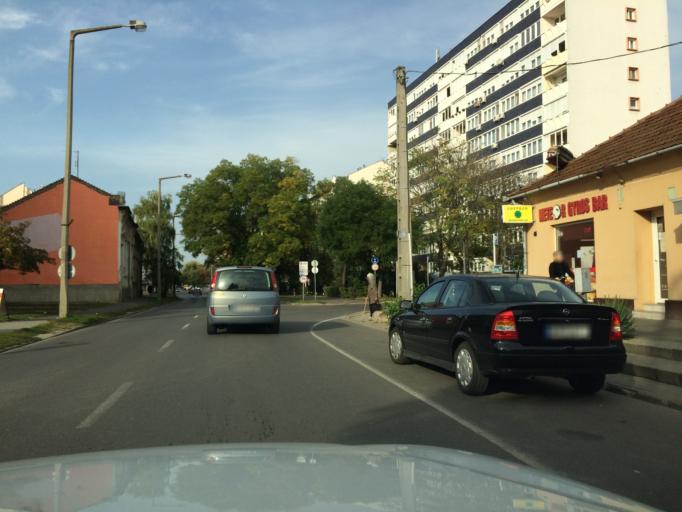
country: HU
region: Szabolcs-Szatmar-Bereg
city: Nyiregyhaza
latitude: 47.9615
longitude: 21.7145
